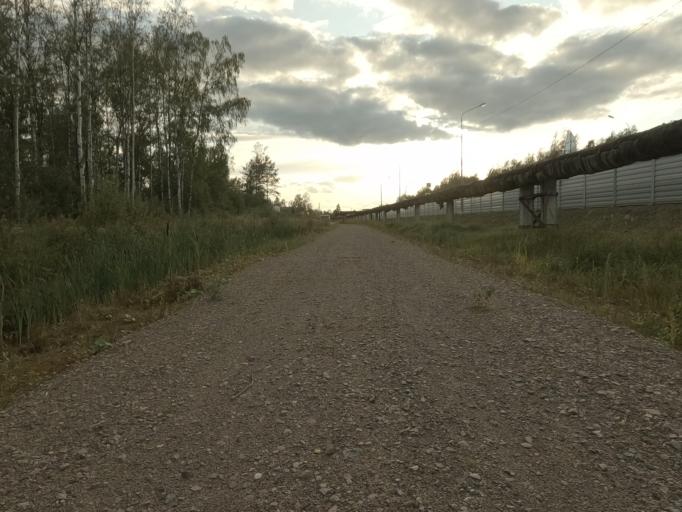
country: RU
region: Leningrad
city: Mga
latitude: 59.7572
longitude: 31.0876
